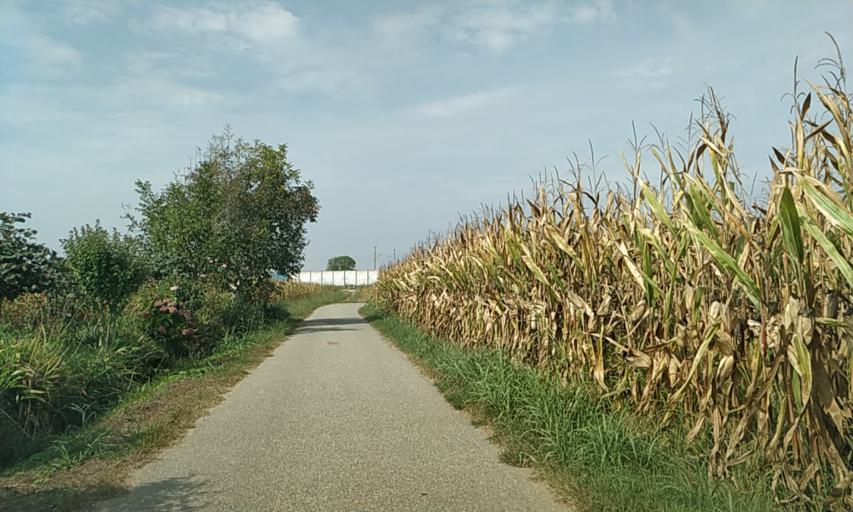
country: IT
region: Piedmont
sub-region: Provincia di Vercelli
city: Livorno Ferraris
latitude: 45.3168
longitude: 8.0711
